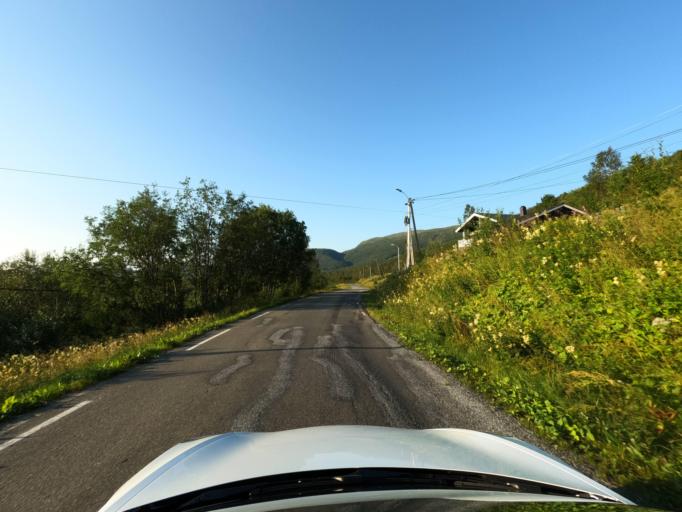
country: NO
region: Nordland
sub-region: Ballangen
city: Ballangen
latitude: 68.5196
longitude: 16.7580
